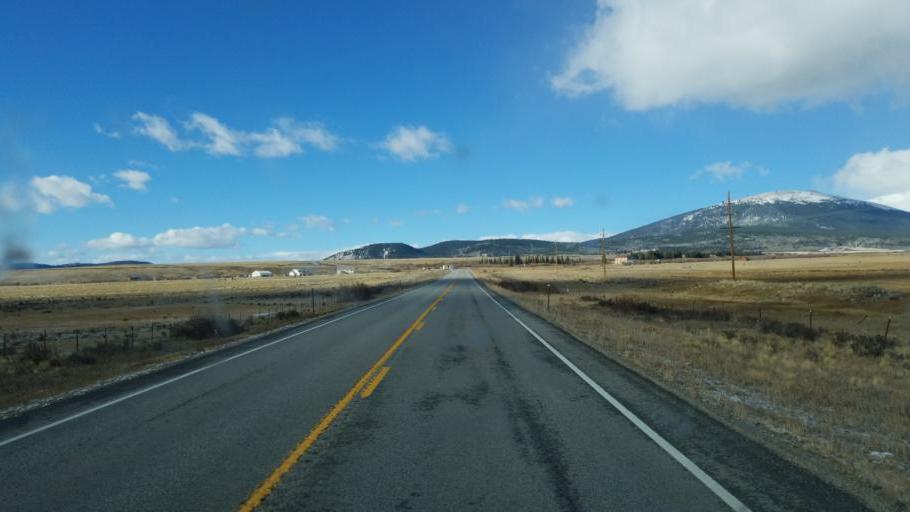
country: US
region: Colorado
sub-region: Park County
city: Fairplay
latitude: 39.3368
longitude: -105.8602
